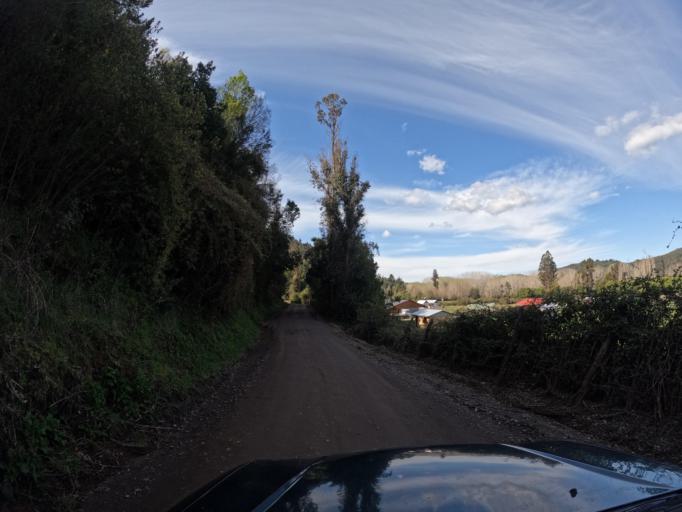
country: CL
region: Biobio
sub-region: Provincia de Concepcion
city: Chiguayante
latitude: -37.0699
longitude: -72.9050
